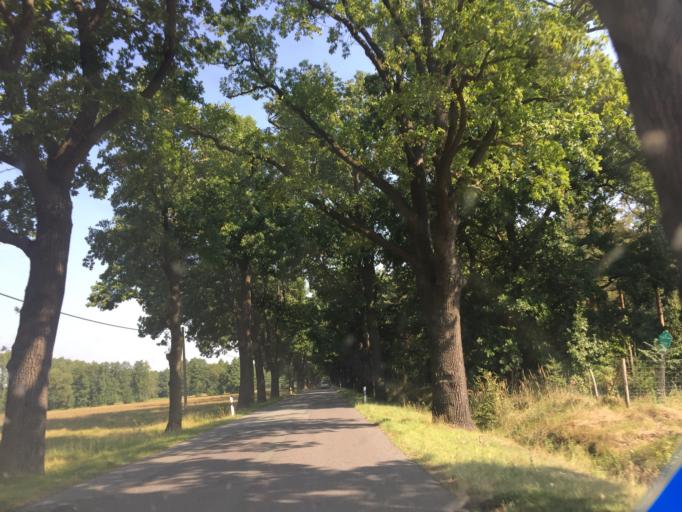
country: DE
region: Saxony
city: Uhyst
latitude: 51.3420
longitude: 14.5037
